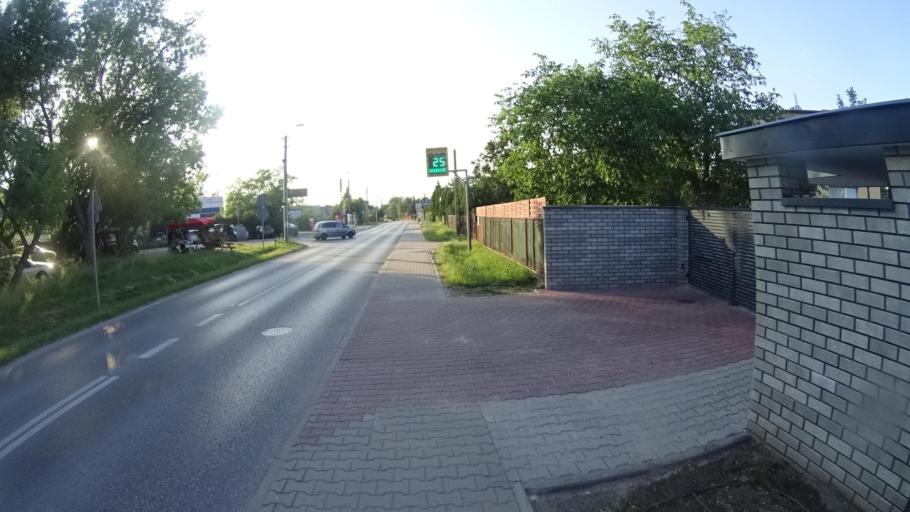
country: PL
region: Masovian Voivodeship
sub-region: Powiat warszawski zachodni
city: Stare Babice
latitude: 52.2554
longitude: 20.8391
